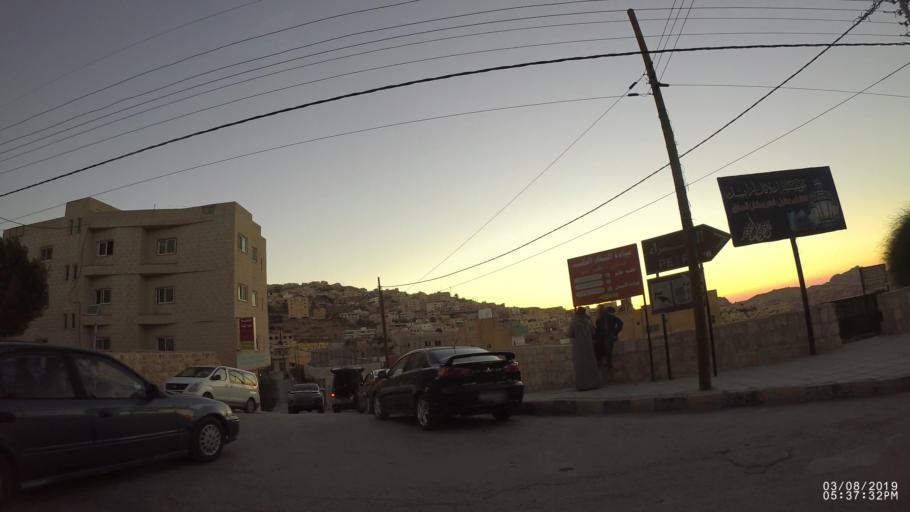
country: JO
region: Ma'an
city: Petra
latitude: 30.3222
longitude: 35.4785
